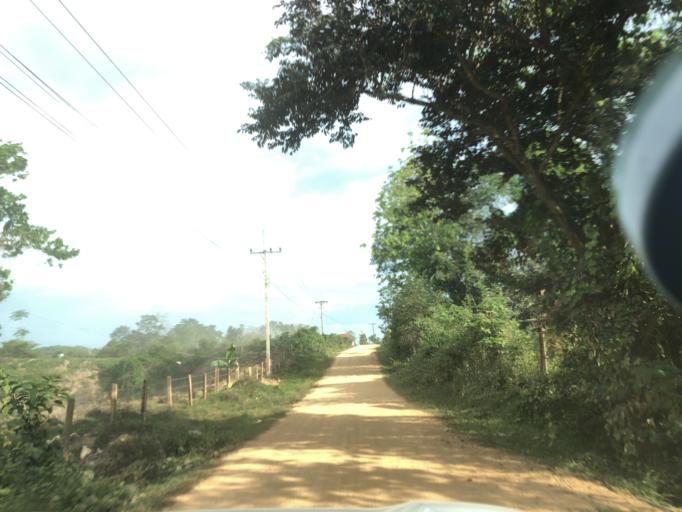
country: TH
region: Loei
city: Chiang Khan
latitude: 18.0119
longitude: 101.4201
